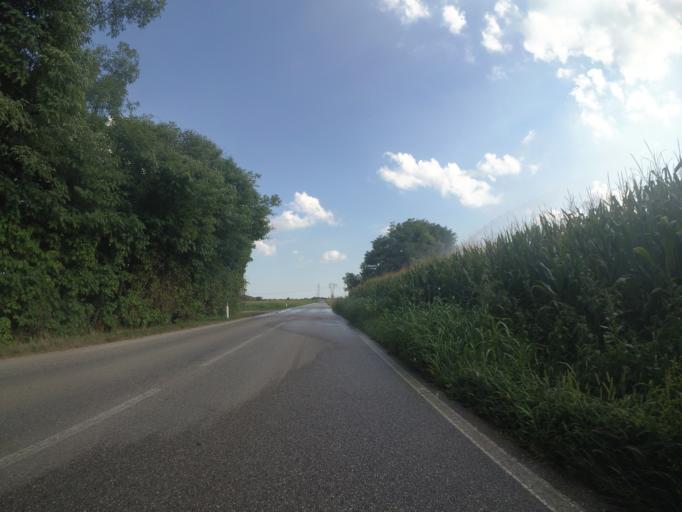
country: IT
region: Friuli Venezia Giulia
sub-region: Provincia di Udine
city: Basiliano-Vissandone
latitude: 46.0518
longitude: 13.0882
